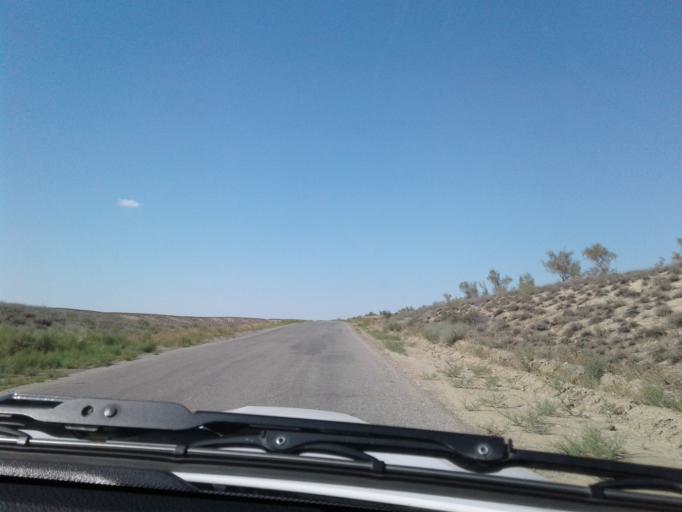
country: TM
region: Balkan
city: Magtymguly
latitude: 38.5742
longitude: 56.1866
